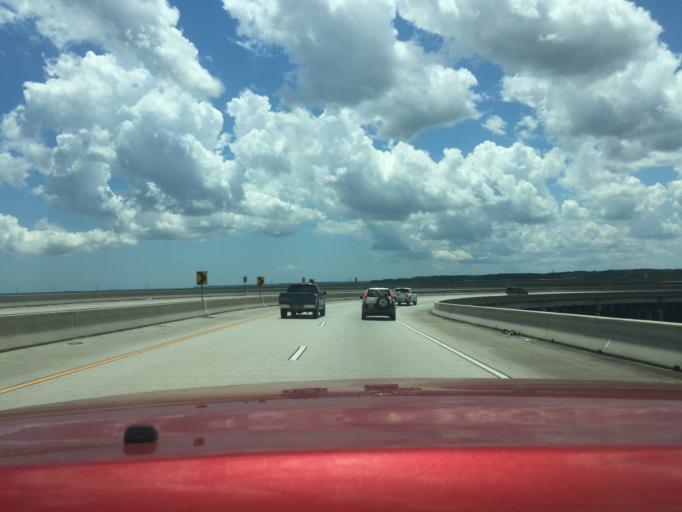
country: US
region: Georgia
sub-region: Chatham County
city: Georgetown
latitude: 31.9837
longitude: -81.2000
